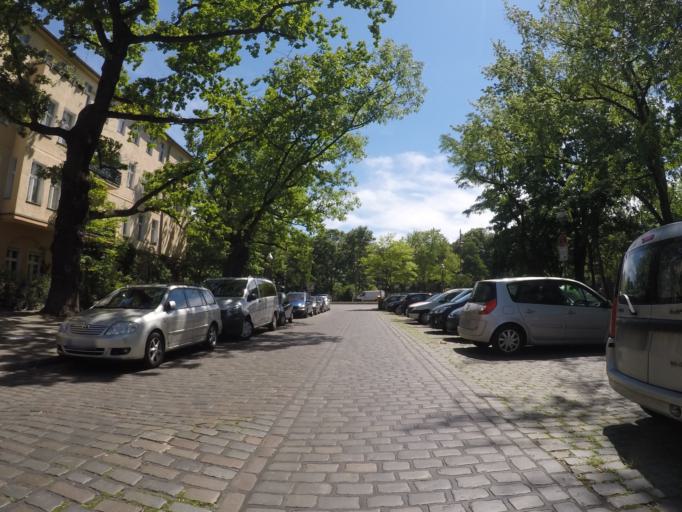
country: DE
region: Berlin
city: Bezirk Kreuzberg
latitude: 52.4889
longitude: 13.4135
